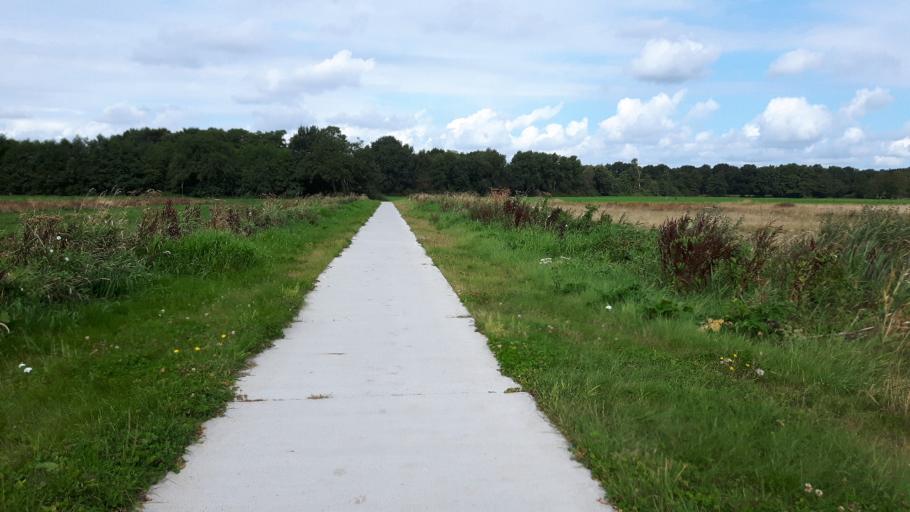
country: NL
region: Groningen
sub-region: Gemeente Leek
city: Leek
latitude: 53.1082
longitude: 6.4407
